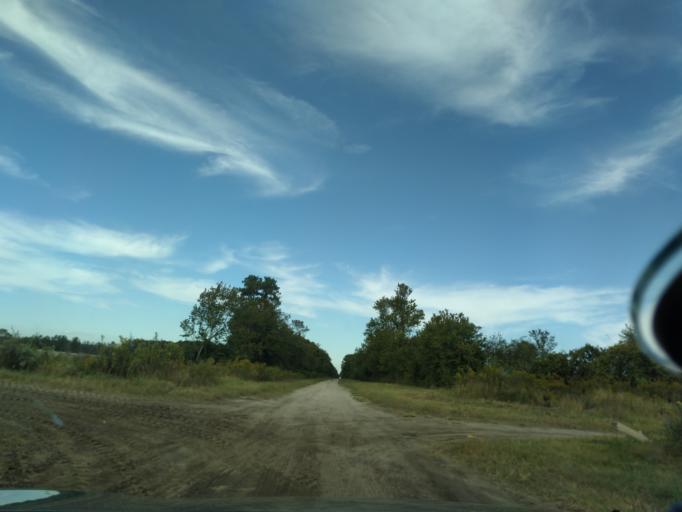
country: US
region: North Carolina
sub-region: Beaufort County
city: Belhaven
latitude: 35.7118
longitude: -76.5841
